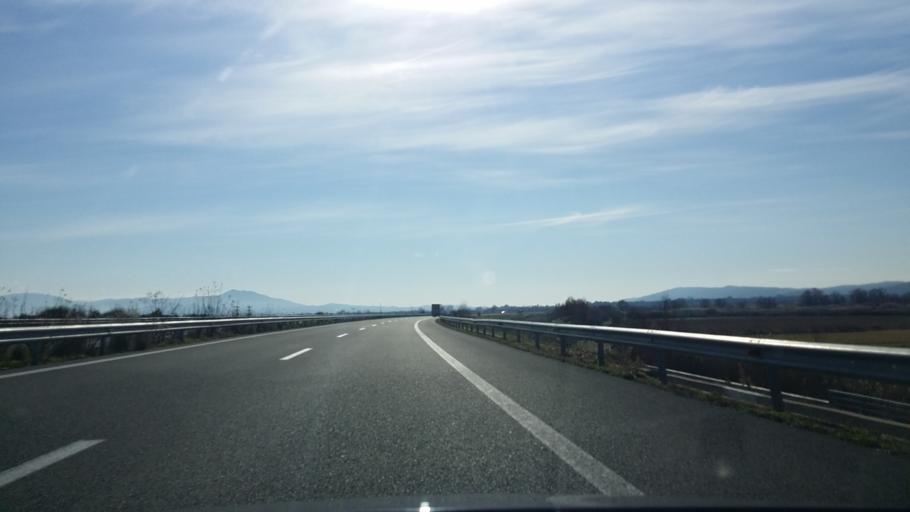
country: GR
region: West Greece
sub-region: Nomos Aitolias kai Akarnanias
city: Lepenou
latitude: 38.6574
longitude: 21.2435
